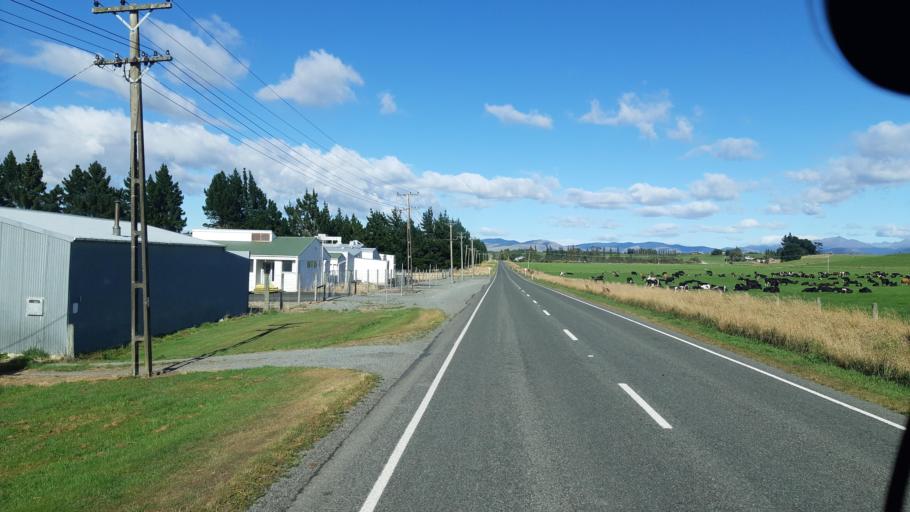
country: NZ
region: Southland
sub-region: Southland District
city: Winton
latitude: -45.6699
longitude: 168.2309
